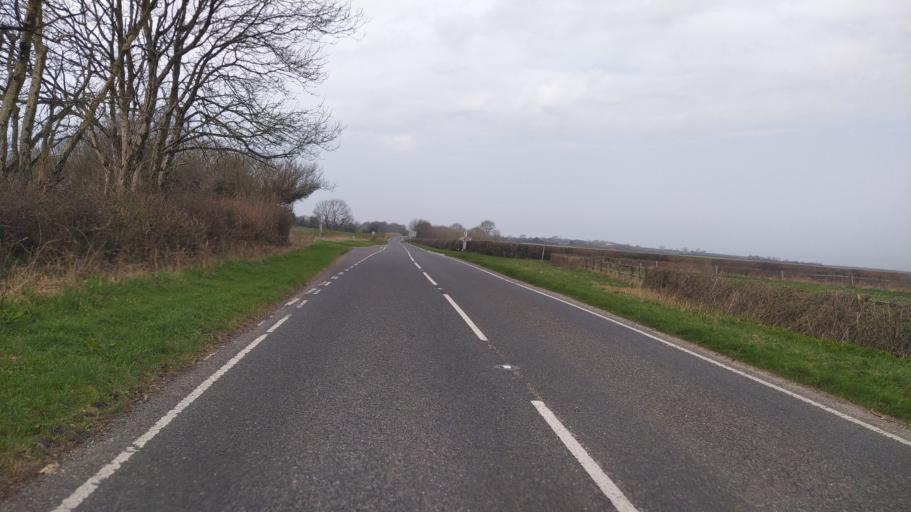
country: GB
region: England
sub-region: Dorset
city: Beaminster
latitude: 50.8255
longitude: -2.6768
